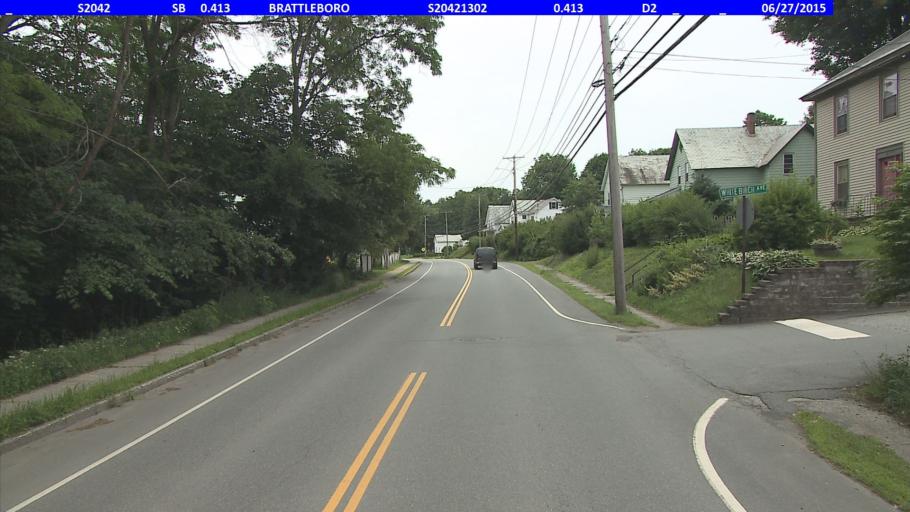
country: US
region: Vermont
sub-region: Windham County
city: Brattleboro
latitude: 42.8432
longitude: -72.5569
